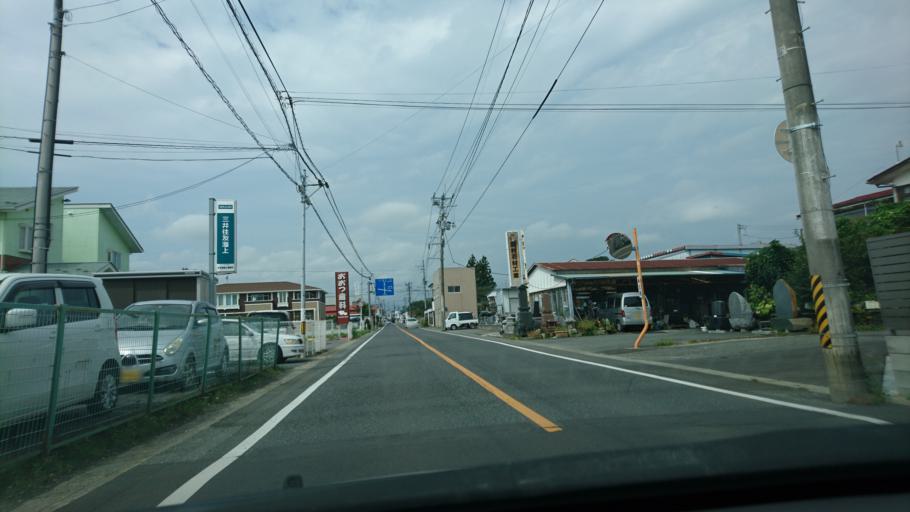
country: JP
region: Miyagi
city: Furukawa
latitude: 38.7345
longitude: 141.0318
